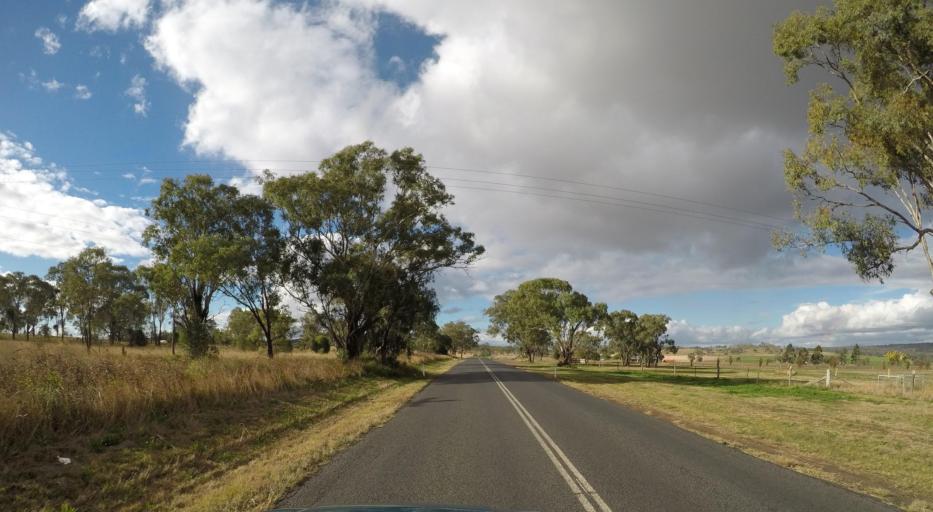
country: AU
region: Queensland
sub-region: Toowoomba
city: Westbrook
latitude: -27.6985
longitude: 151.6648
